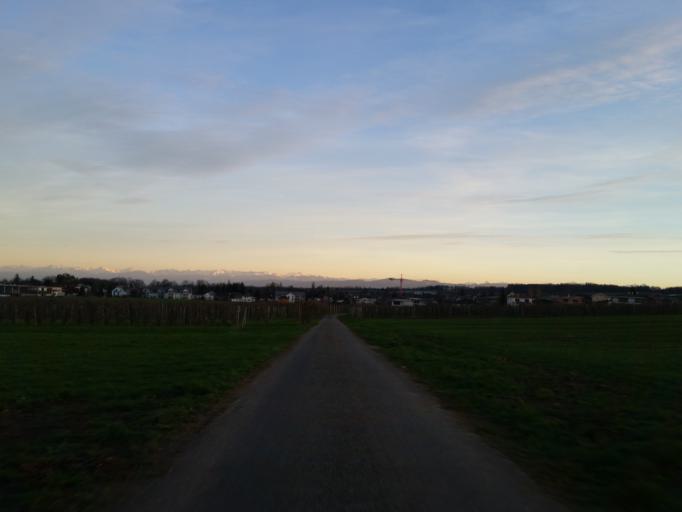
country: CH
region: Thurgau
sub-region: Kreuzlingen District
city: Guttingen
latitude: 47.6109
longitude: 9.2832
